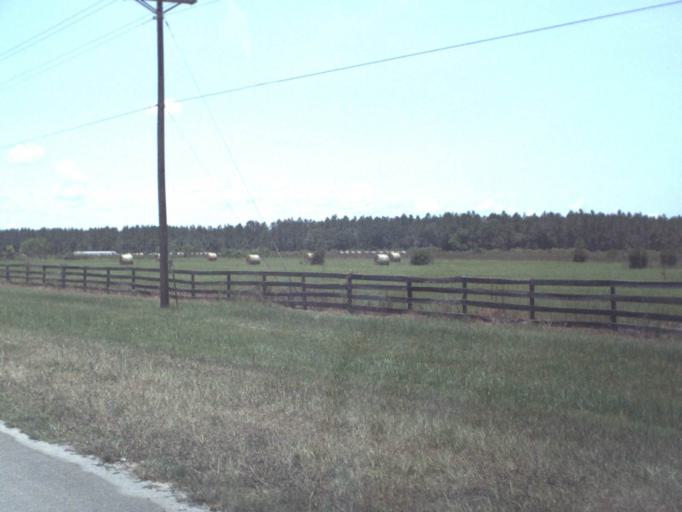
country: US
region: Florida
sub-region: Clay County
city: Keystone Heights
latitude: 29.7135
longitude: -82.0981
